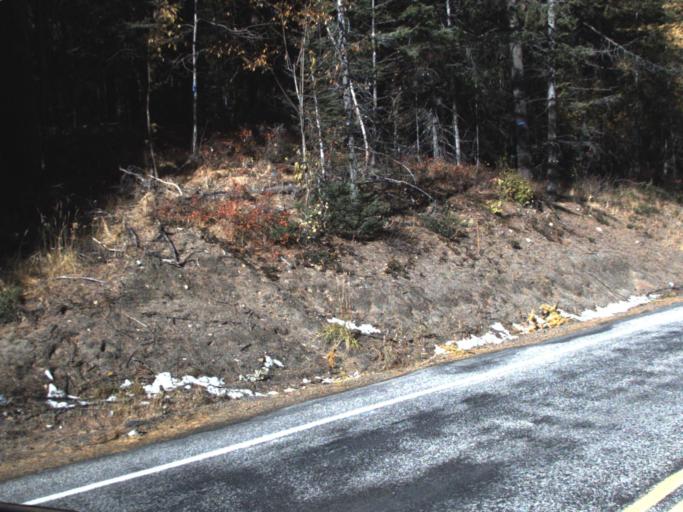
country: US
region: Washington
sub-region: Ferry County
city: Republic
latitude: 48.6166
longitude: -118.4440
